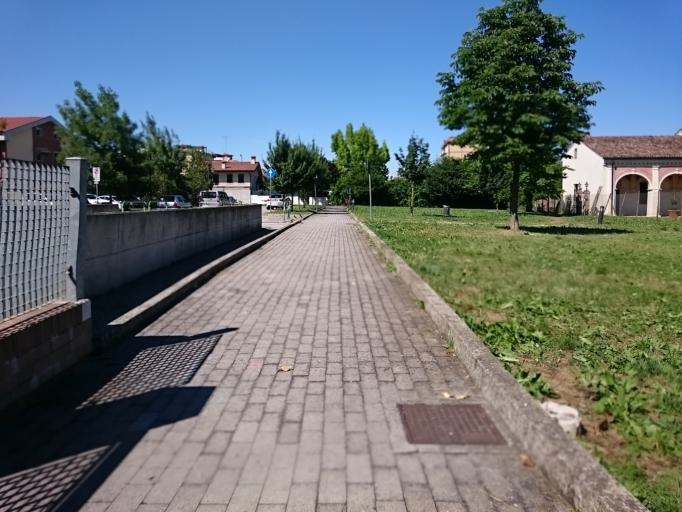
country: IT
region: Veneto
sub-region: Provincia di Padova
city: Piove di Sacco-Piovega
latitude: 45.2989
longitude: 12.0391
